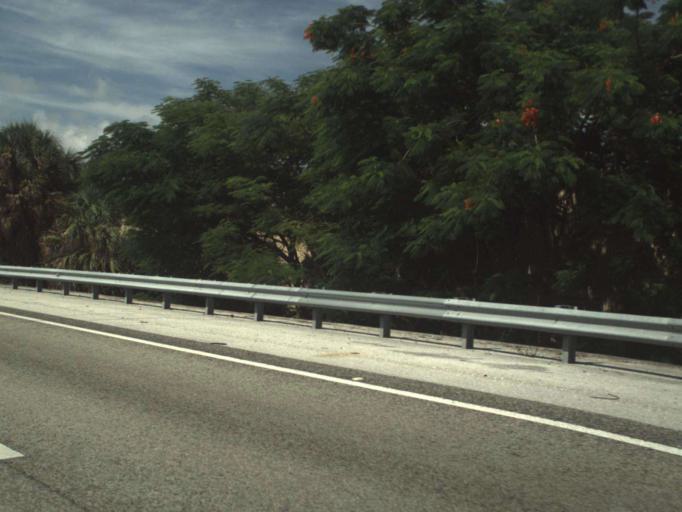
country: US
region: Florida
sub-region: Palm Beach County
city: Schall Circle
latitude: 26.7249
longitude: -80.0917
